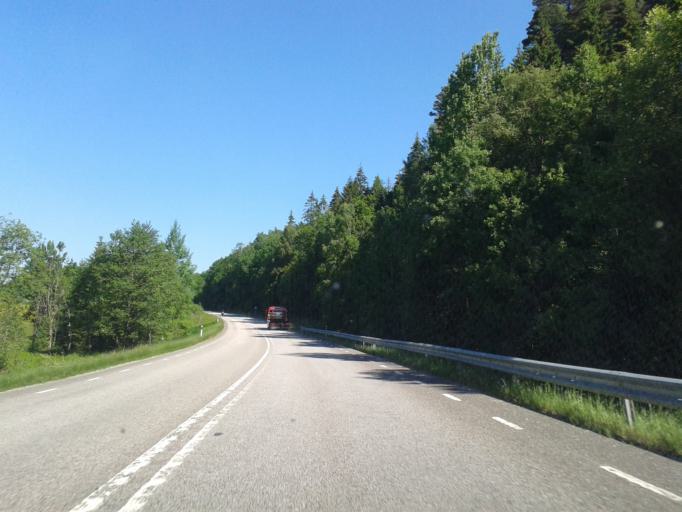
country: SE
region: Vaestra Goetaland
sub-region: Orust
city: Henan
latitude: 58.1951
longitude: 11.6895
